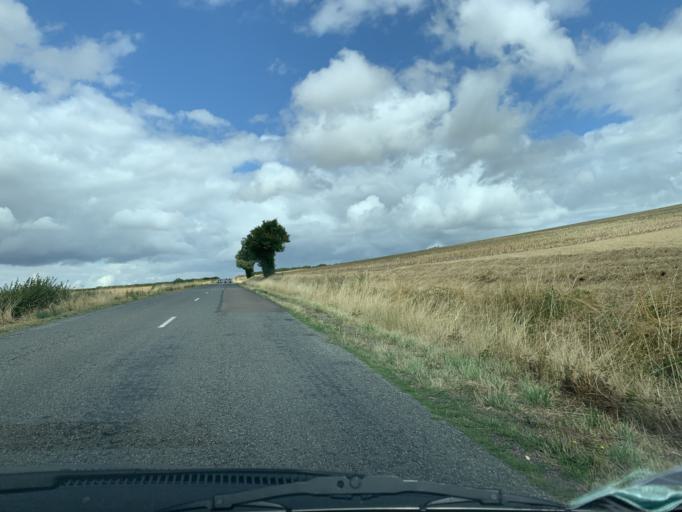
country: FR
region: Bourgogne
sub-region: Departement de la Nievre
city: Clamecy
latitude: 47.4056
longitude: 3.4512
